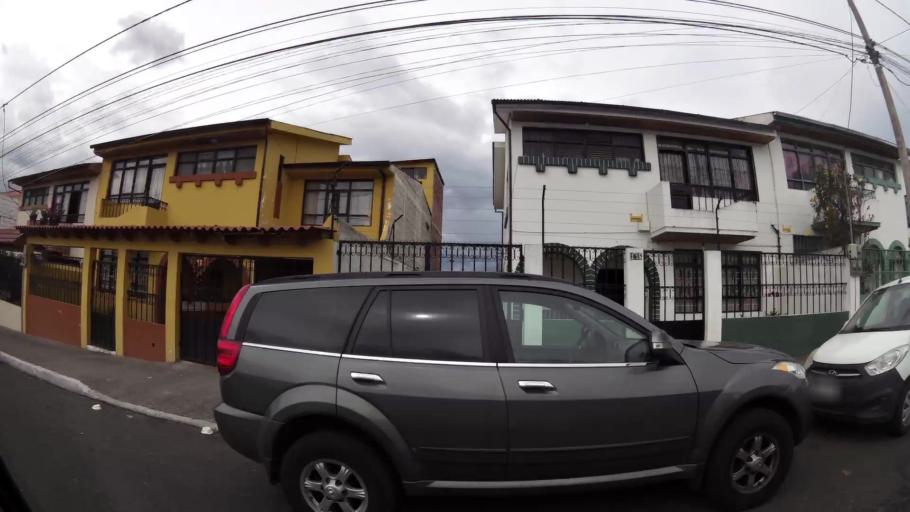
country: EC
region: Tungurahua
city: Ambato
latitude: -1.2552
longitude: -78.6217
